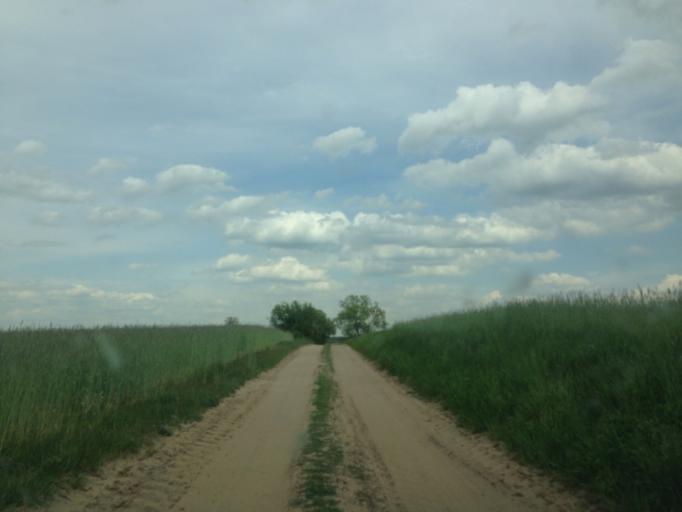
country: PL
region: Kujawsko-Pomorskie
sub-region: Powiat brodnicki
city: Bobrowo
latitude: 53.2524
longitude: 19.2922
